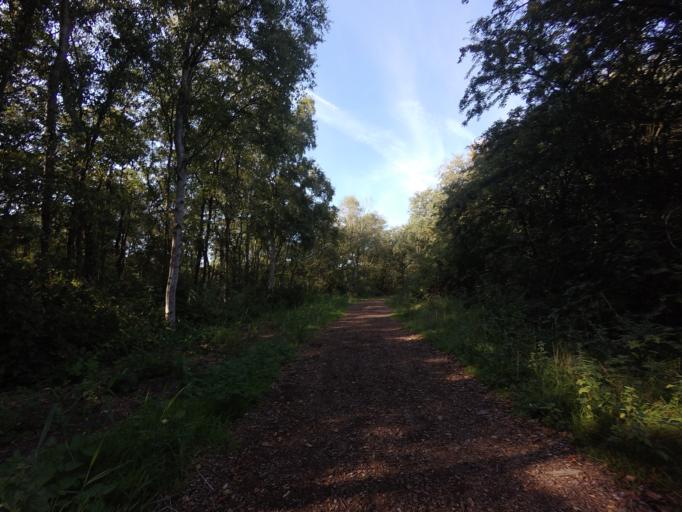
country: NL
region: Friesland
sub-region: Gemeente Schiermonnikoog
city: Schiermonnikoog
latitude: 53.4895
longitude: 6.1732
